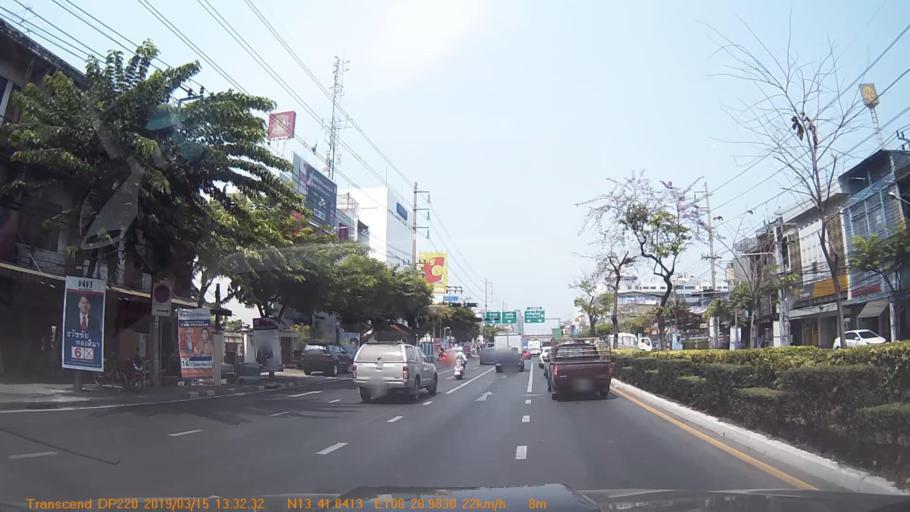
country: TH
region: Bangkok
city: Bang Kho Laem
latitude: 13.6974
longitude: 100.4831
